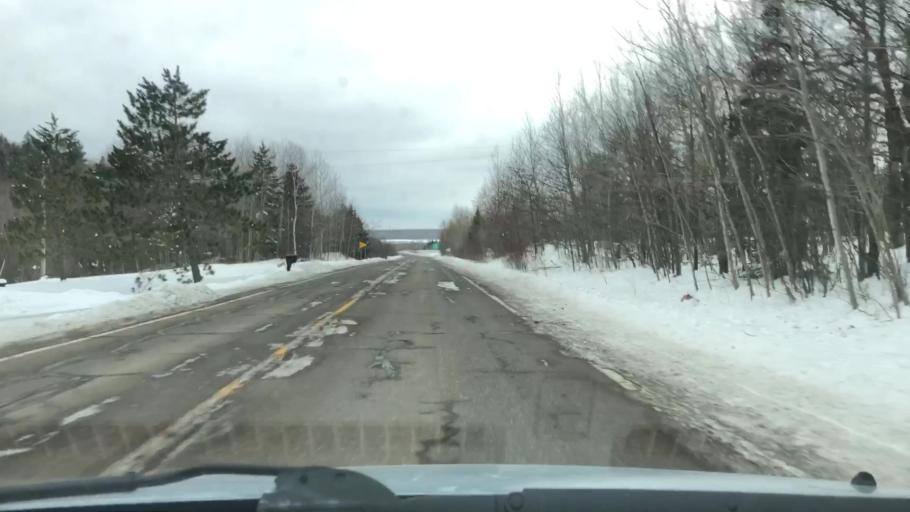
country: US
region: Minnesota
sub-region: Saint Louis County
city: Proctor
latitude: 46.7104
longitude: -92.2660
